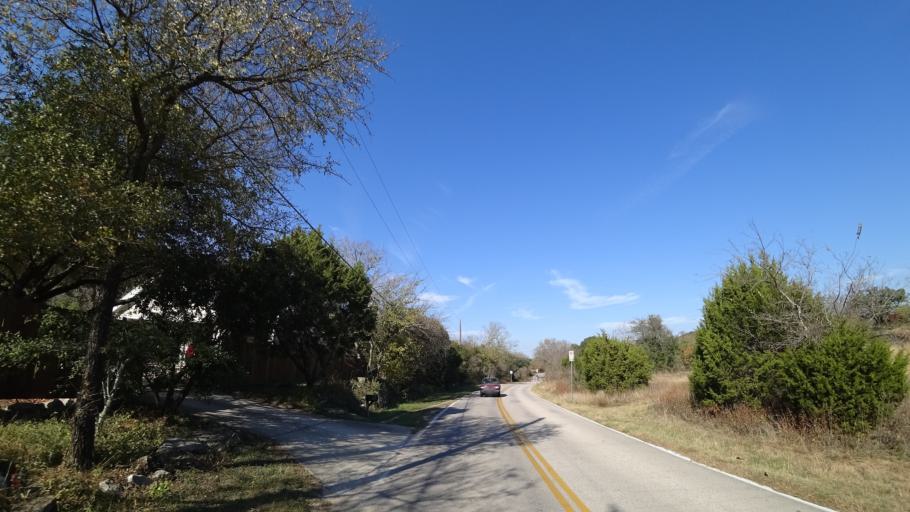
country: US
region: Texas
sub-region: Williamson County
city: Jollyville
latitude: 30.3982
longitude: -97.7820
